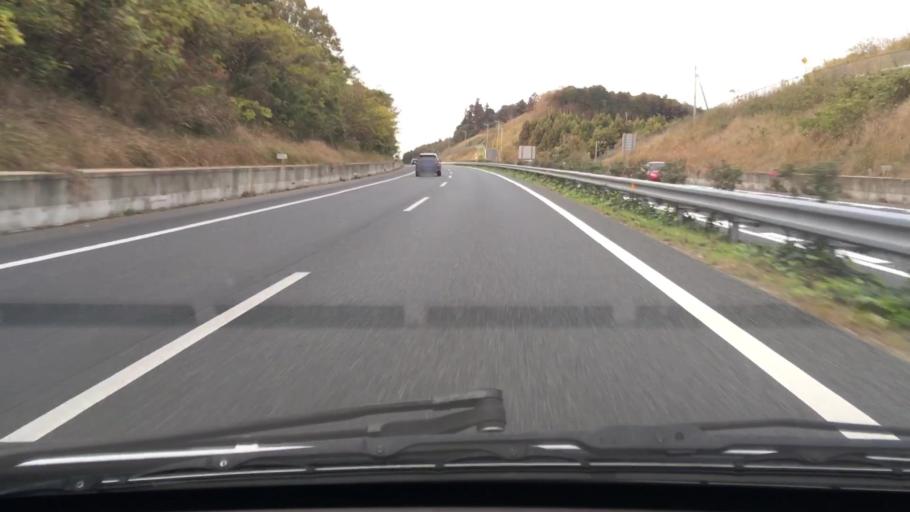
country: JP
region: Chiba
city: Kisarazu
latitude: 35.3282
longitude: 139.9463
